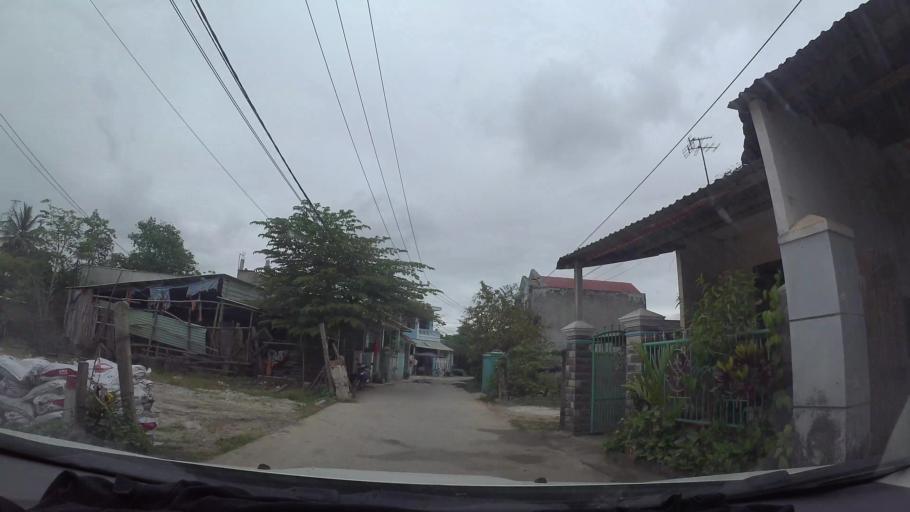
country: VN
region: Da Nang
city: Lien Chieu
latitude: 16.0864
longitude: 108.1025
